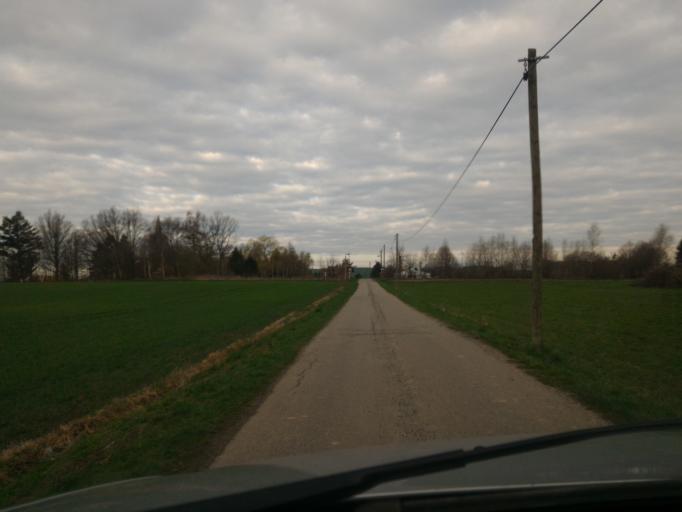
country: DE
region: Saxony
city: Leutersdorf
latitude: 50.9608
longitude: 14.6574
